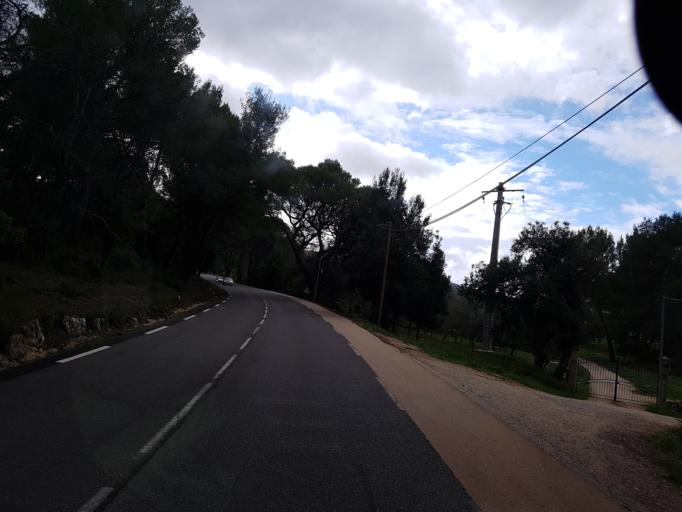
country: FR
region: Provence-Alpes-Cote d'Azur
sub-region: Departement des Bouches-du-Rhone
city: Cuges-les-Pins
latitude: 43.2720
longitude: 5.7187
